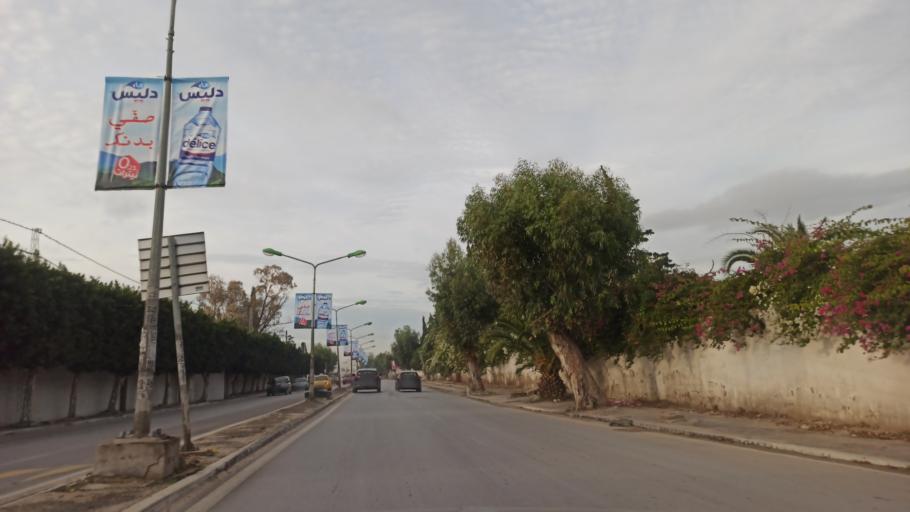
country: TN
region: Ariana
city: Ariana
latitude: 36.8728
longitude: 10.2355
